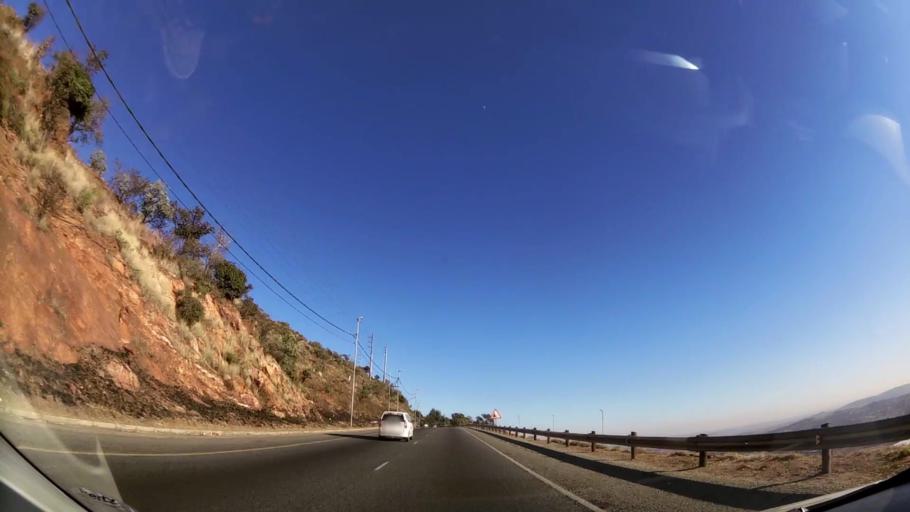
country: ZA
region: Gauteng
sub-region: West Rand District Municipality
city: Muldersdriseloop
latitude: -26.0638
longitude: 27.8109
